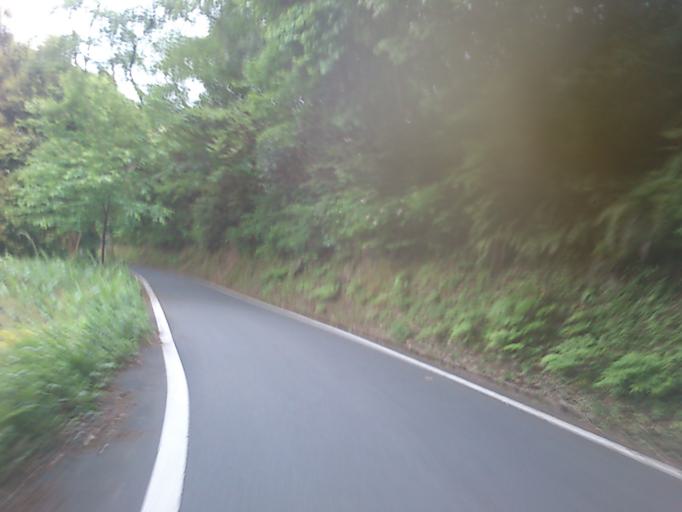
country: JP
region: Kyoto
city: Miyazu
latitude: 35.5662
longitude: 135.1424
